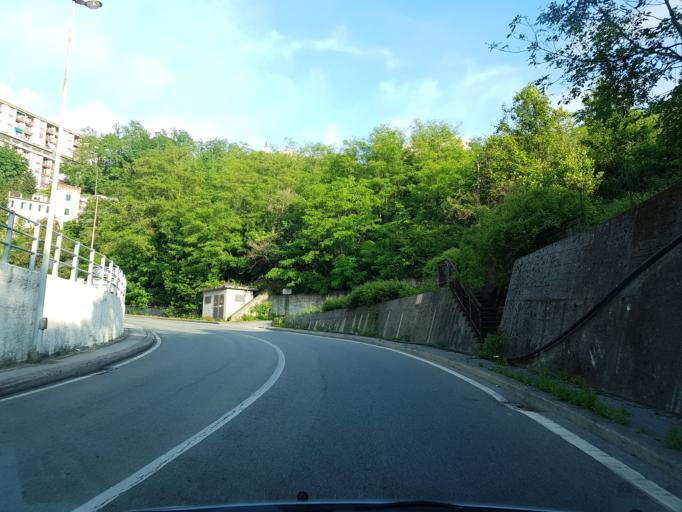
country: IT
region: Liguria
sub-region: Provincia di Genova
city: Genoa
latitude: 44.4517
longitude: 8.9037
